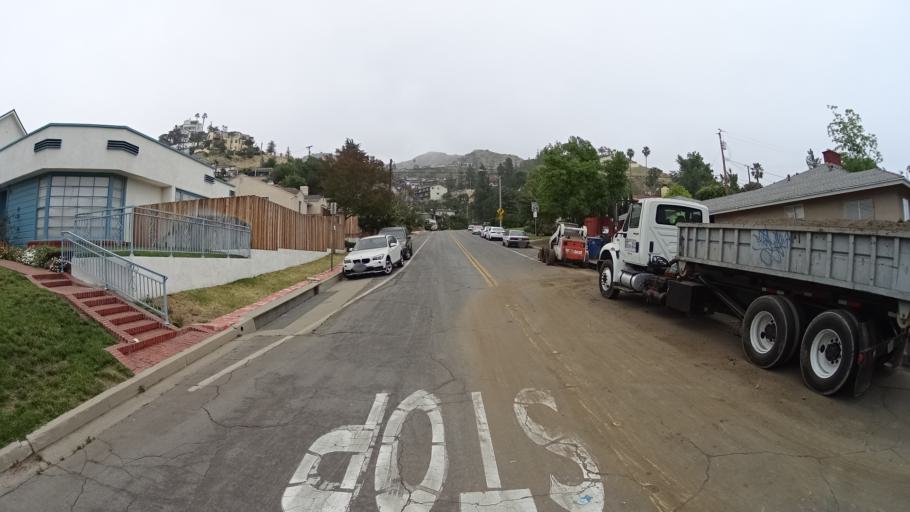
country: US
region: California
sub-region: Los Angeles County
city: Burbank
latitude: 34.1910
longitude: -118.2943
